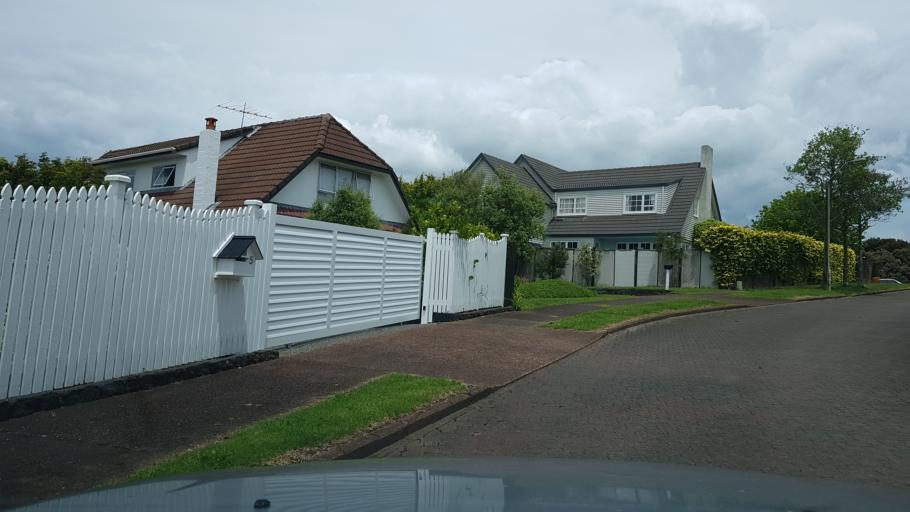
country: NZ
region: Auckland
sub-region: Auckland
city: North Shore
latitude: -36.8201
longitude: 174.7090
